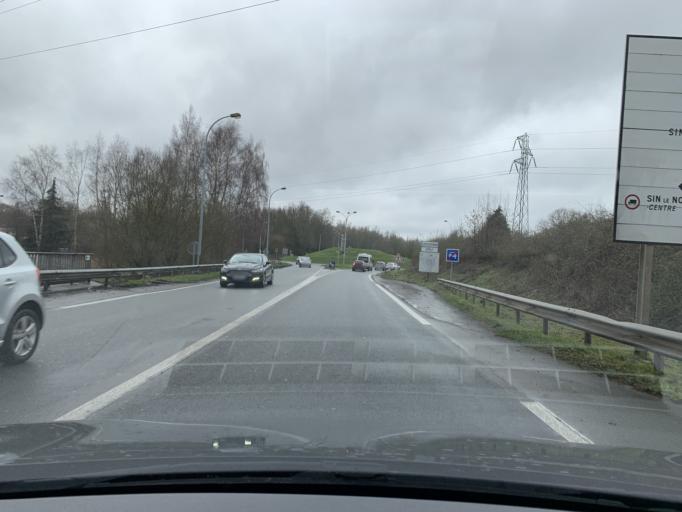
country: FR
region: Nord-Pas-de-Calais
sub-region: Departement du Nord
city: Sin-le-Noble
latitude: 50.3674
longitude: 3.1213
